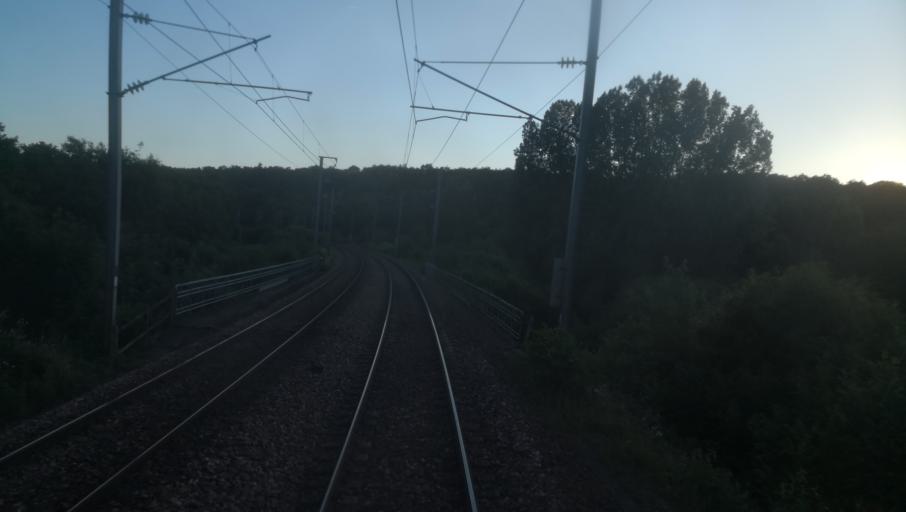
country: FR
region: Haute-Normandie
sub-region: Departement de l'Eure
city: Conches-en-Ouche
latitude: 48.9765
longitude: 0.9681
